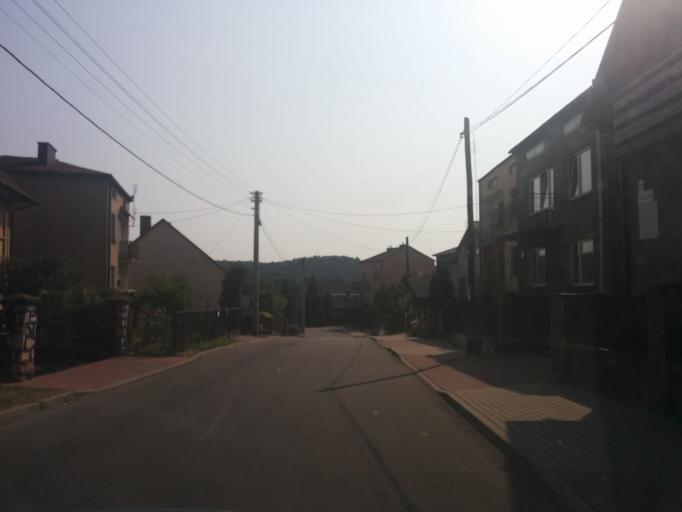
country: PL
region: Silesian Voivodeship
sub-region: Powiat zawiercianski
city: Kroczyce
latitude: 50.5632
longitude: 19.5333
